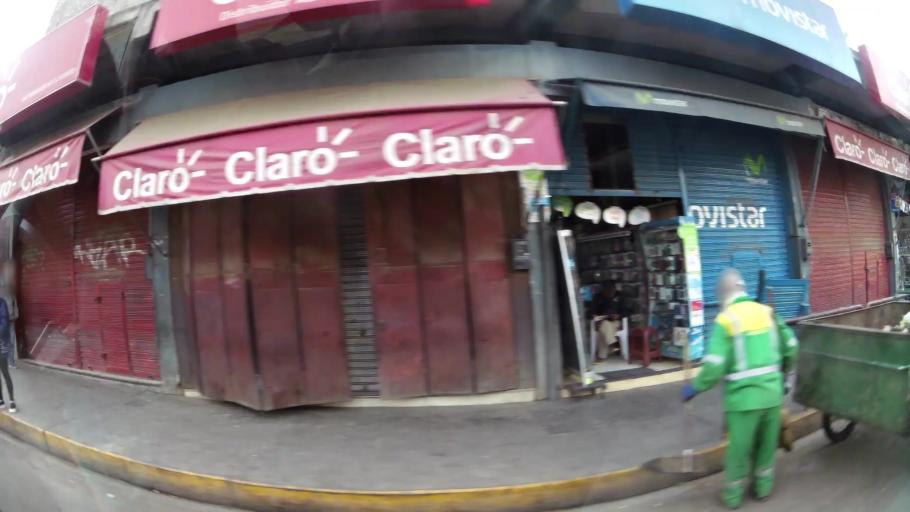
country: PE
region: Junin
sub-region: Provincia de Huancayo
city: Huancayo
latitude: -12.0685
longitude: -75.2051
